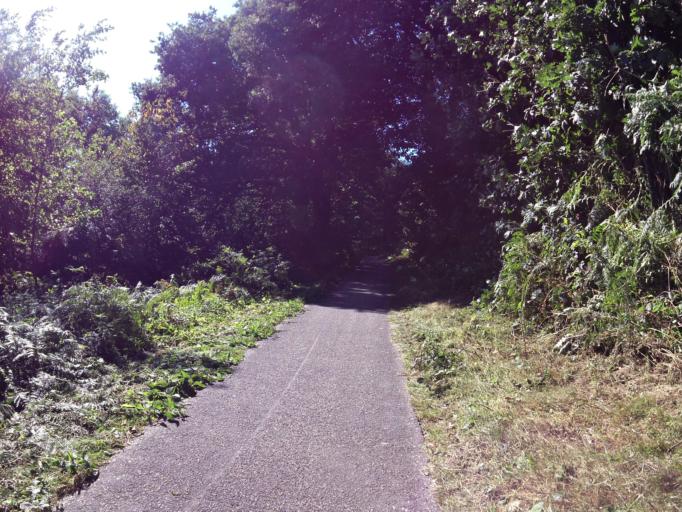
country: NL
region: Gelderland
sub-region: Gemeente Groesbeek
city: Bredeweg
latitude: 51.7385
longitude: 5.9679
